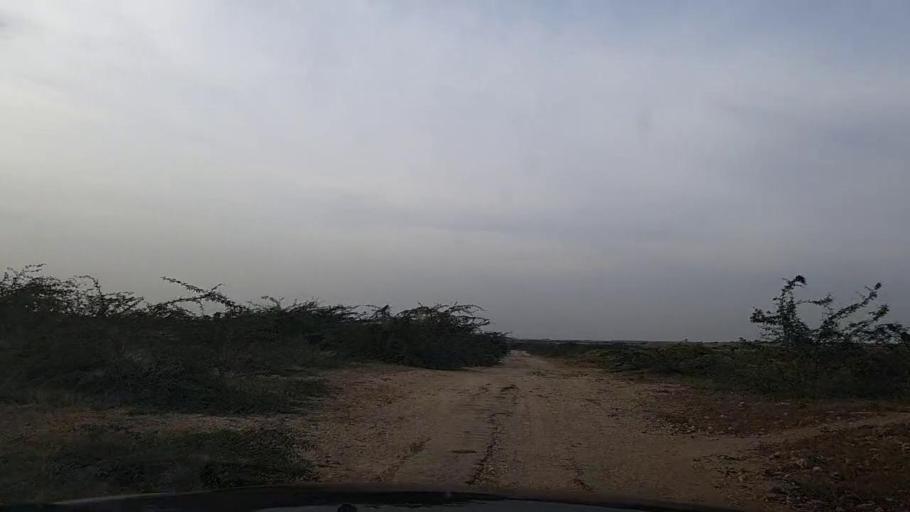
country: PK
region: Sindh
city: Gharo
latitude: 24.7875
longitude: 67.5564
